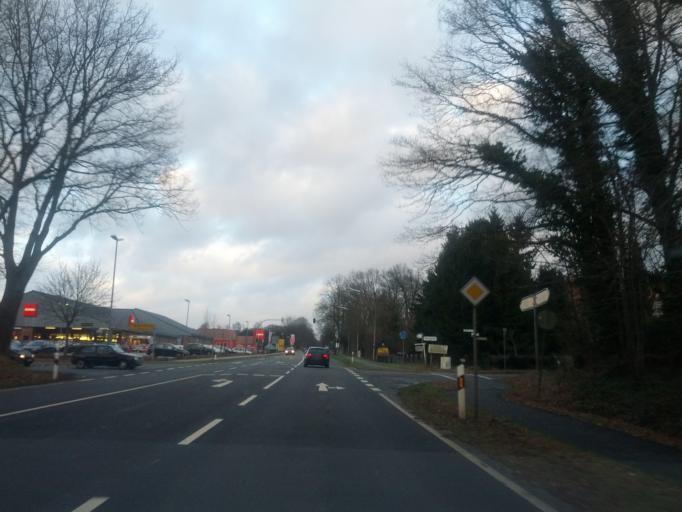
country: DE
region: Lower Saxony
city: Scheessel
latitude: 53.1608
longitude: 9.4736
